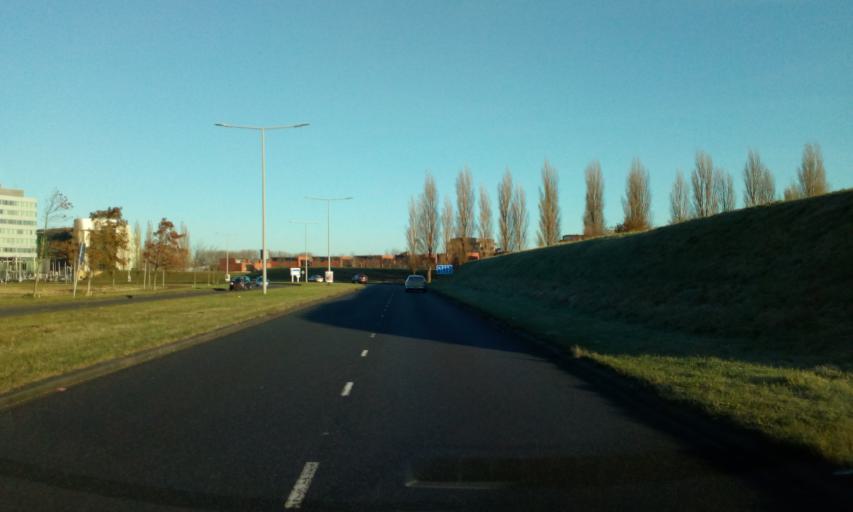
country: NL
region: South Holland
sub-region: Gemeente Leidschendam-Voorburg
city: Voorburg
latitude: 52.0689
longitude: 4.3997
